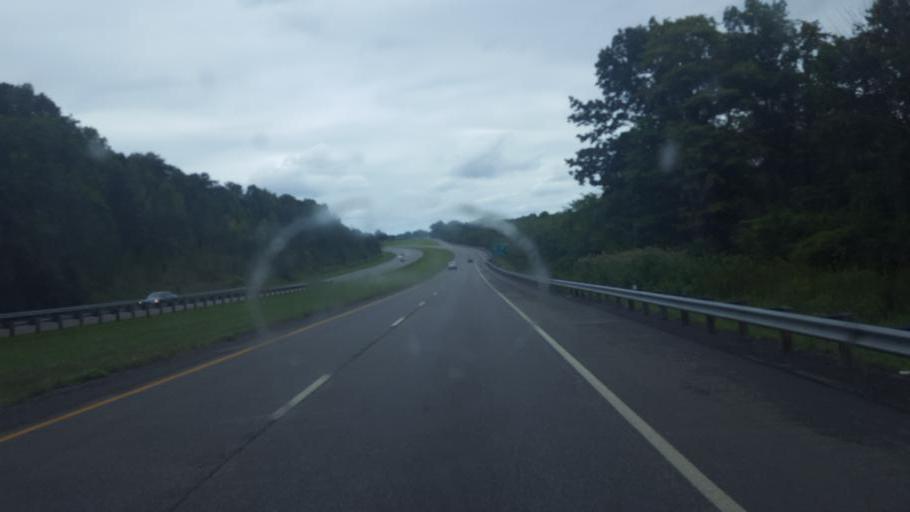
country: US
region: Ohio
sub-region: Lake County
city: Painesville
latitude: 41.6863
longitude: -81.2549
